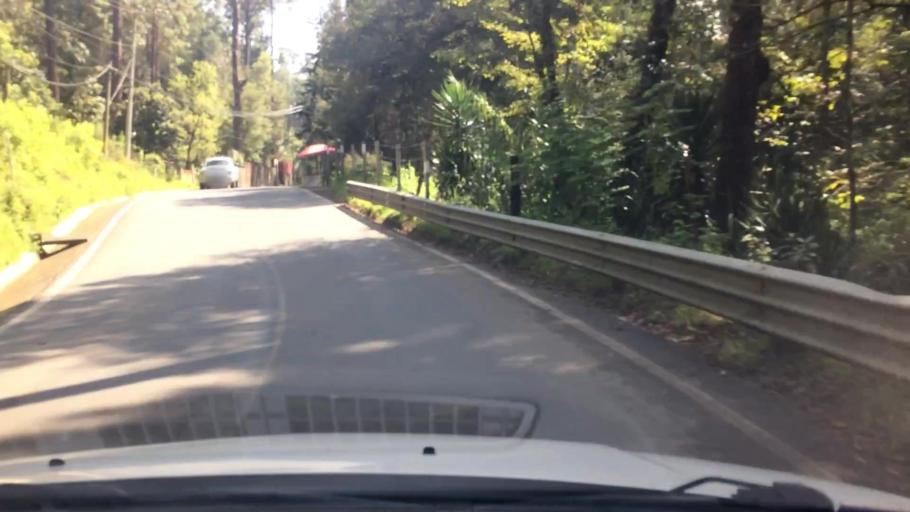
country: MX
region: Mexico
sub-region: Valle de Bravo
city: Casas Viejas
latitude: 19.1739
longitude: -100.1108
